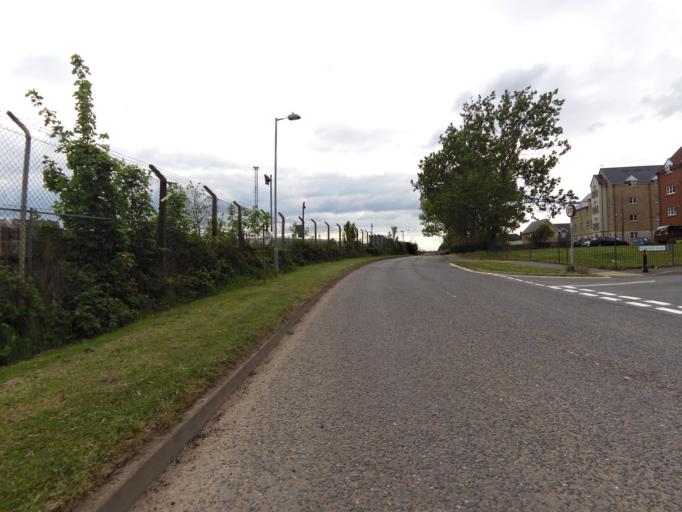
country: GB
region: England
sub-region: Suffolk
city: Ipswich
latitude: 52.0348
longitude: 1.1726
